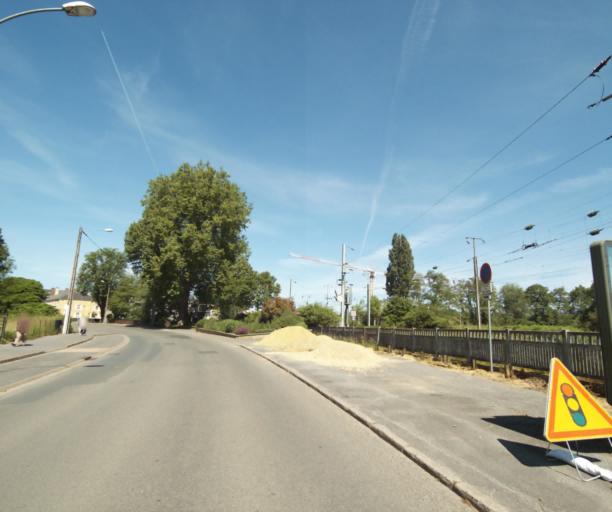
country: FR
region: Champagne-Ardenne
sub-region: Departement des Ardennes
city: Villers-Semeuse
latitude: 49.7516
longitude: 4.7348
